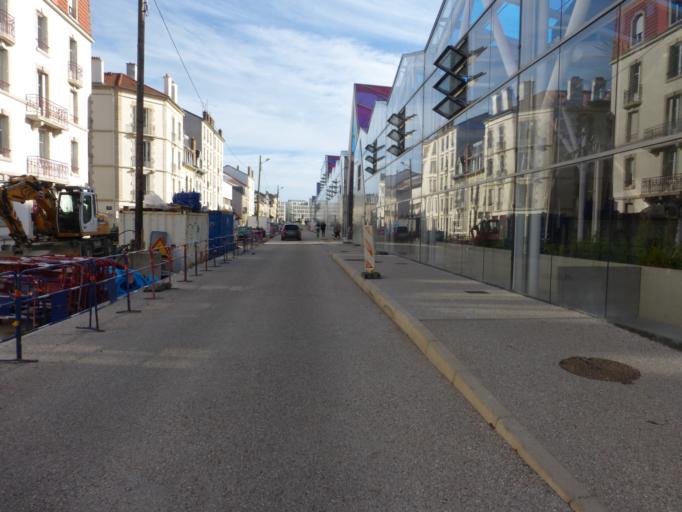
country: FR
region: Lorraine
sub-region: Departement de Meurthe-et-Moselle
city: Nancy
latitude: 48.6748
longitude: 6.1705
